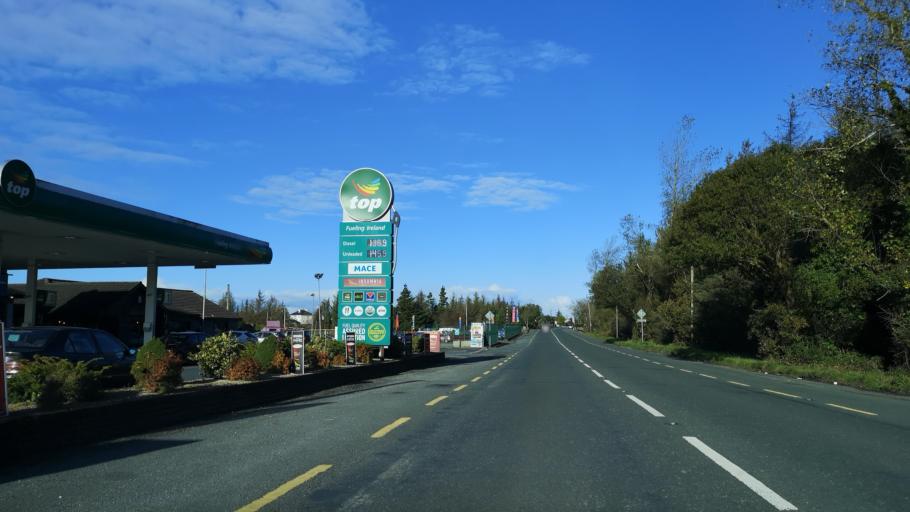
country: IE
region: Connaught
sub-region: County Galway
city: Moycullen
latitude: 53.4498
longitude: -9.0915
